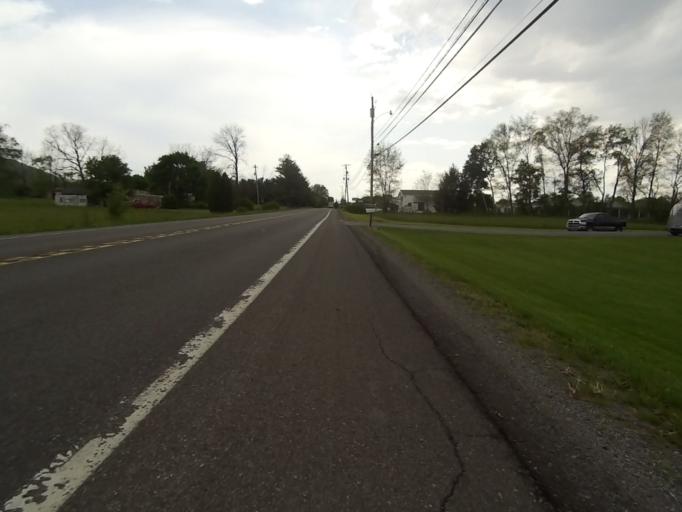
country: US
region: Pennsylvania
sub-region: Centre County
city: Zion
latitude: 40.9404
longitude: -77.6424
